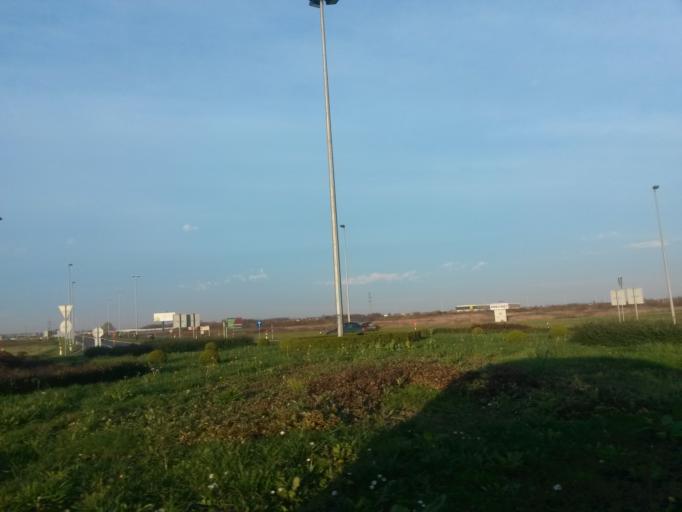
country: HR
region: Varazdinska
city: Jalkovec
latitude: 46.2655
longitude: 16.3626
